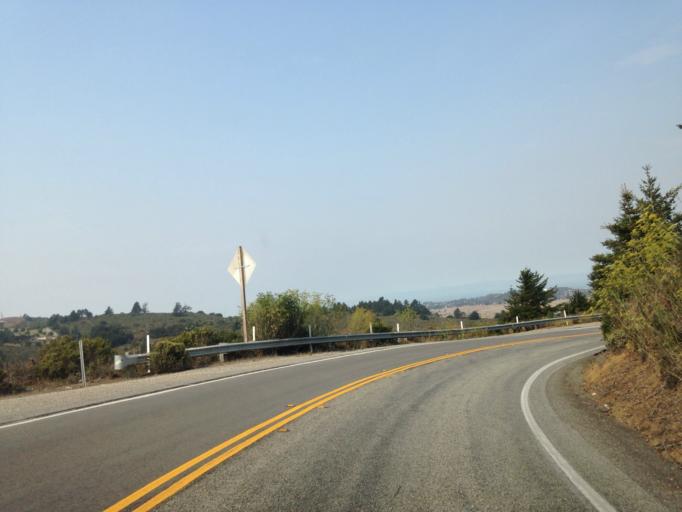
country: US
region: California
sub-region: San Mateo County
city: Highlands-Baywood Park
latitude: 37.4905
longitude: -122.3664
